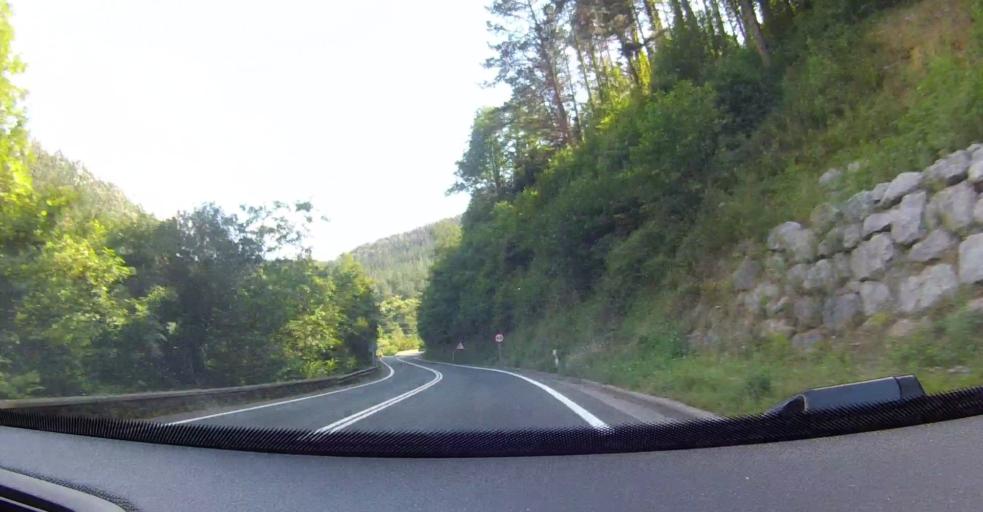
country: ES
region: Basque Country
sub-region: Bizkaia
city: Muxika
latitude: 43.2637
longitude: -2.6859
